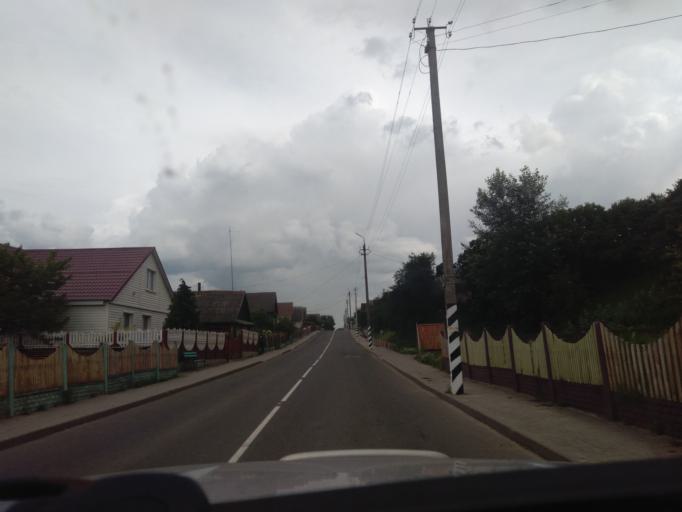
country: BY
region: Minsk
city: Kapyl'
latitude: 53.1557
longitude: 27.0846
